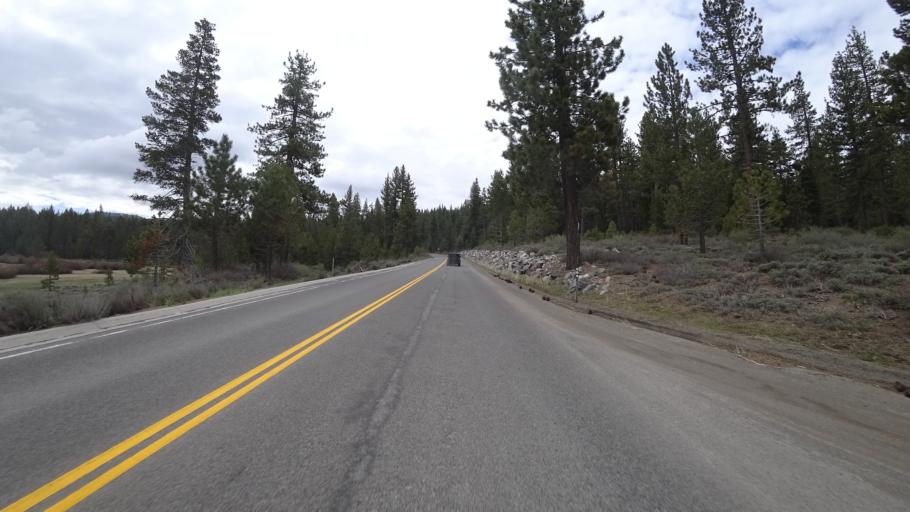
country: US
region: Nevada
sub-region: Douglas County
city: Kingsbury
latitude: 39.1103
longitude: -119.9224
